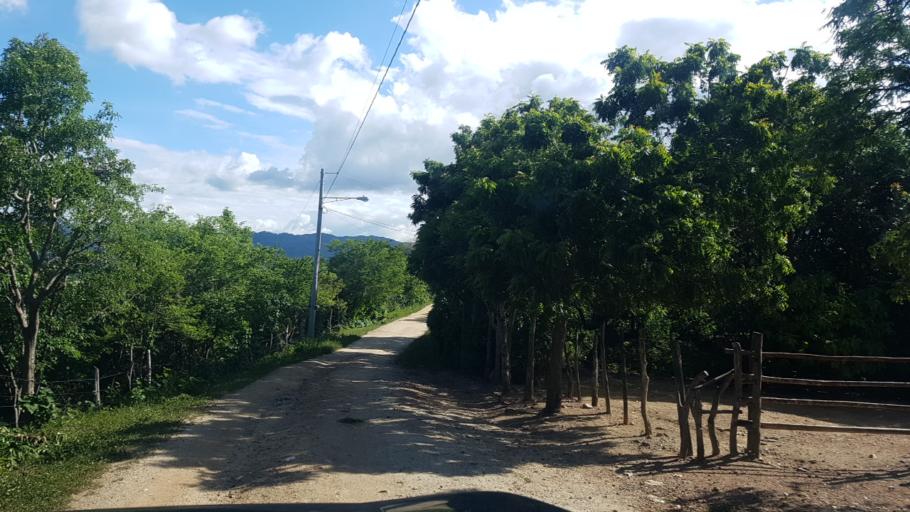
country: NI
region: Nueva Segovia
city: Mozonte
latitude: 13.6364
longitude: -86.3986
